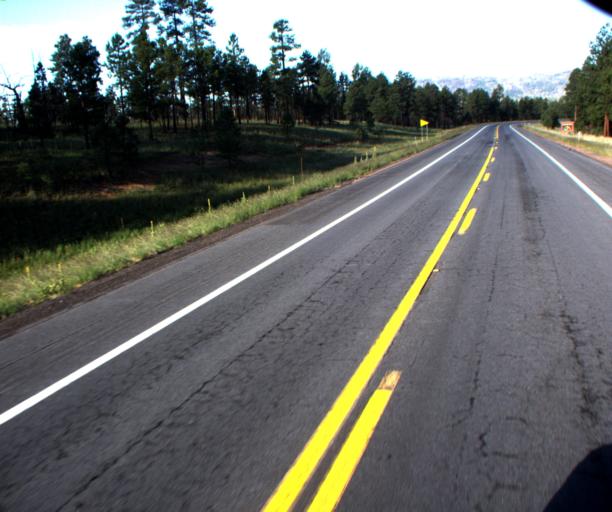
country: US
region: New Mexico
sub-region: Catron County
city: Reserve
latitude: 33.8128
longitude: -109.0621
